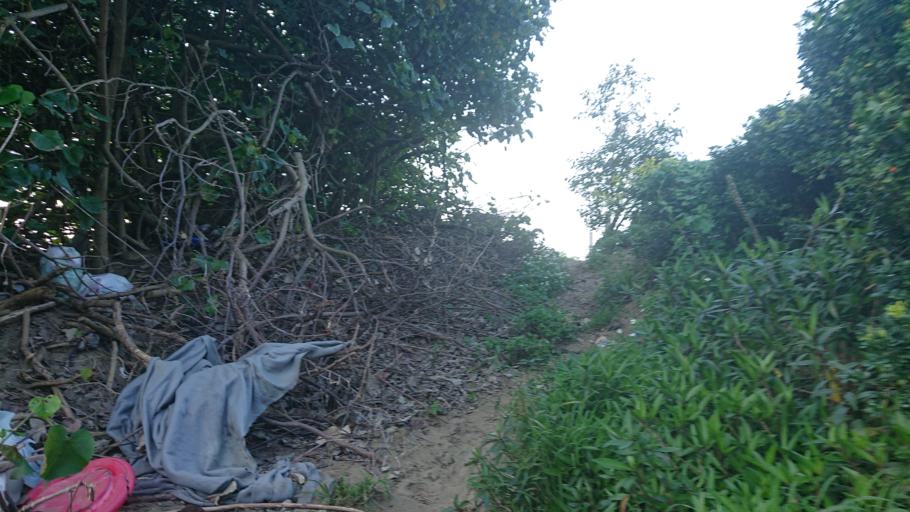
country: TW
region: Taipei
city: Taipei
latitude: 25.1903
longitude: 121.4183
